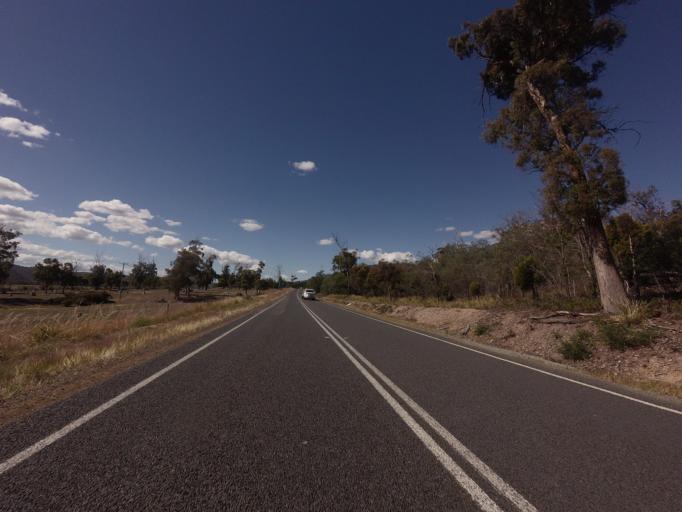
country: AU
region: Tasmania
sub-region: Break O'Day
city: St Helens
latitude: -41.6840
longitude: 147.8839
